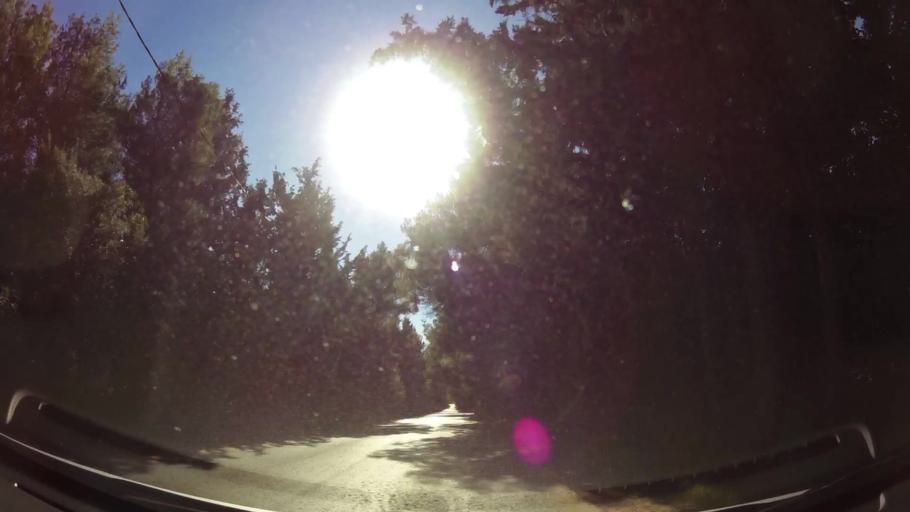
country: GR
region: Attica
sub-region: Nomarchia Anatolikis Attikis
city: Varybobi
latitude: 38.1154
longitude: 23.8008
